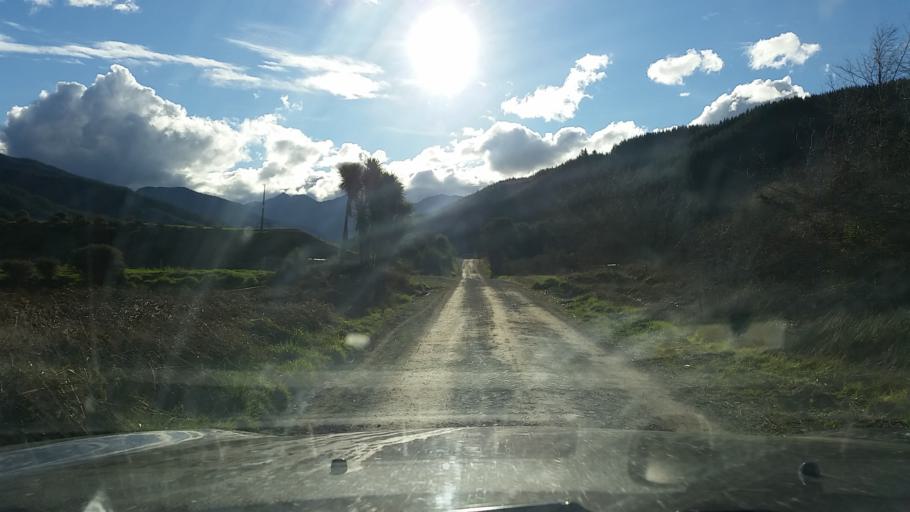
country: NZ
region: Nelson
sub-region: Nelson City
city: Nelson
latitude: -41.5667
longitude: 173.4499
